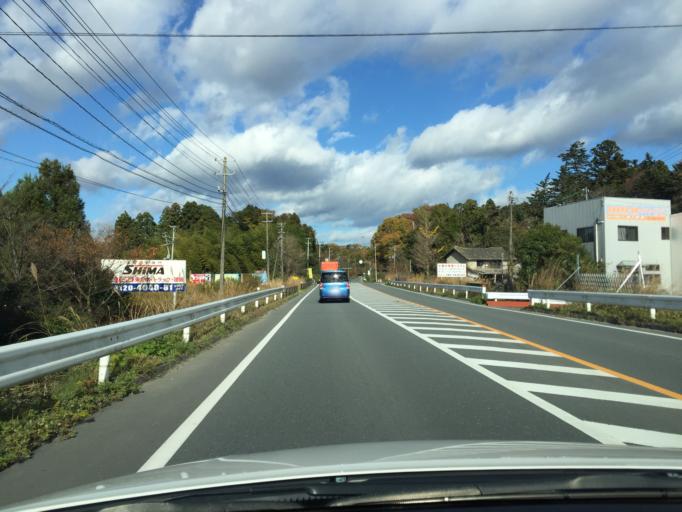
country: JP
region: Fukushima
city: Namie
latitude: 37.4702
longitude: 141.0089
